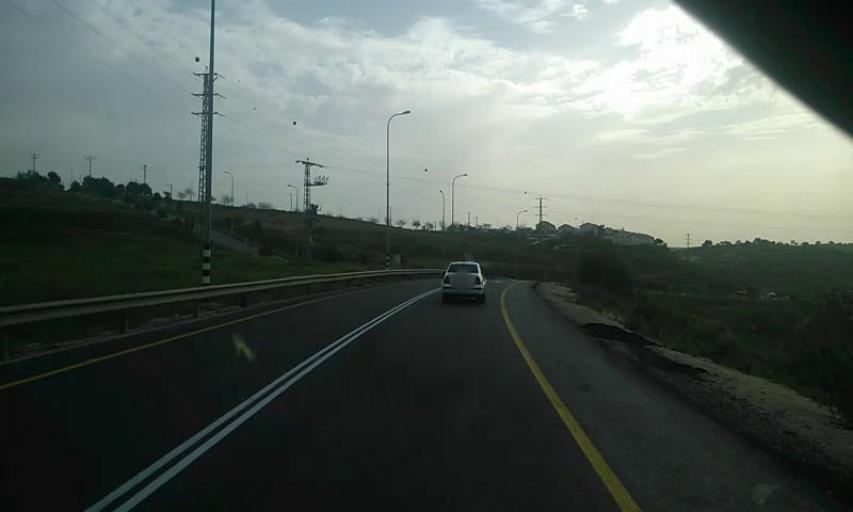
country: PS
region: West Bank
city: Jit
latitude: 32.2092
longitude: 35.1625
